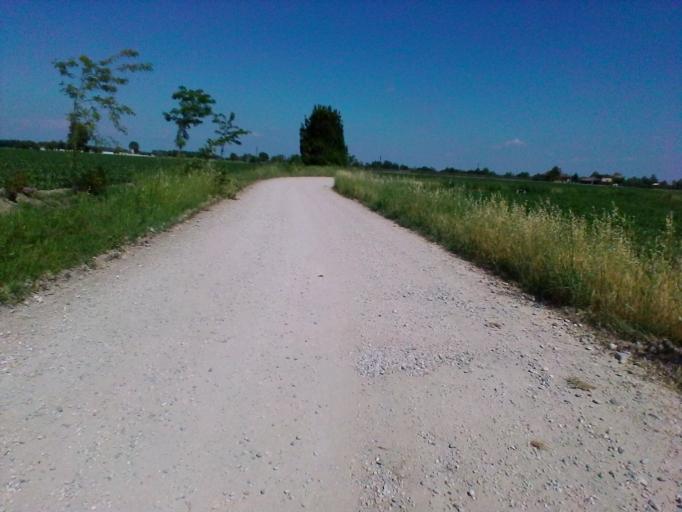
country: IT
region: Veneto
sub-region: Provincia di Verona
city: Povegliano Veronese
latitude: 45.3281
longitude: 10.8772
